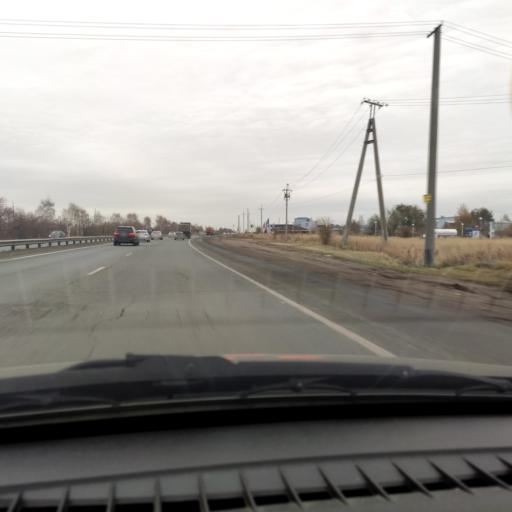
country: RU
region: Samara
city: Tol'yatti
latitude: 53.5788
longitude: 49.4090
